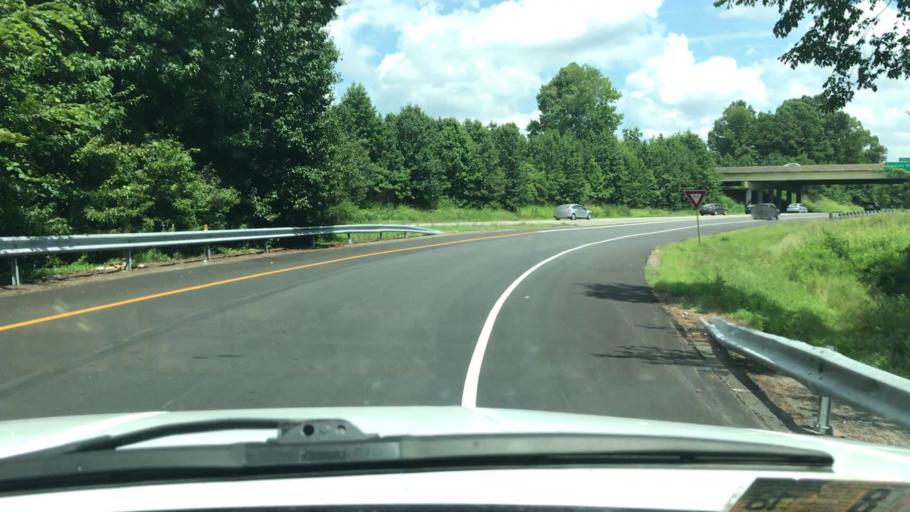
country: US
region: Virginia
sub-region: Henrico County
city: Short Pump
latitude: 37.6352
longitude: -77.5765
